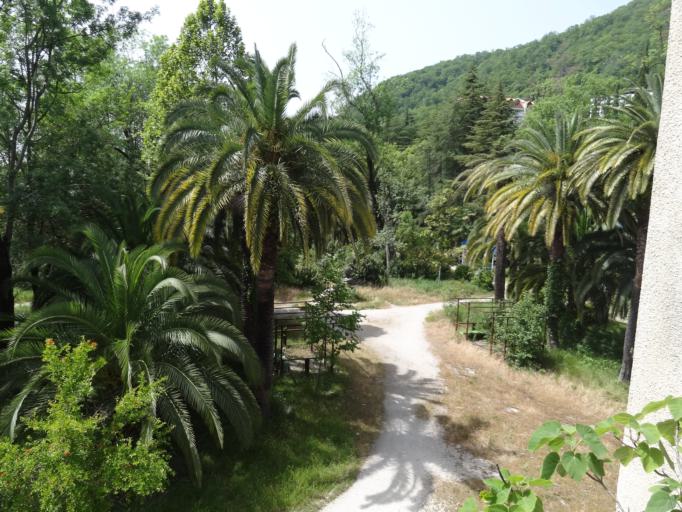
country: GE
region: Abkhazia
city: Gagra
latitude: 43.3222
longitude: 40.2355
